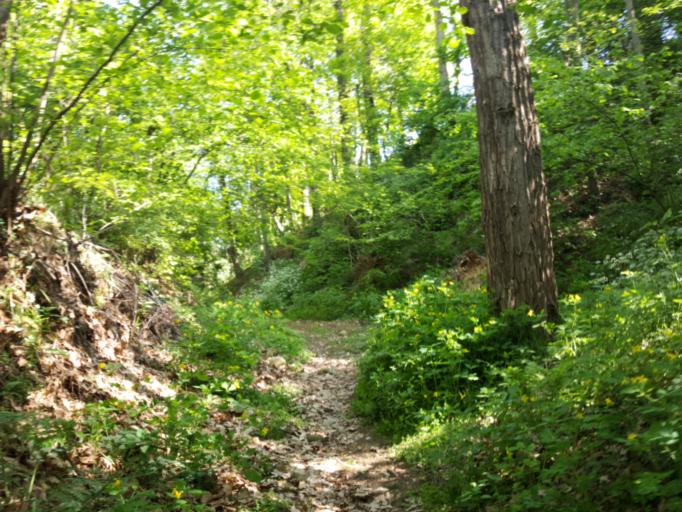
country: IT
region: Lombardy
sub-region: Provincia di Como
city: Novedrate
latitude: 45.6919
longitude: 9.1218
